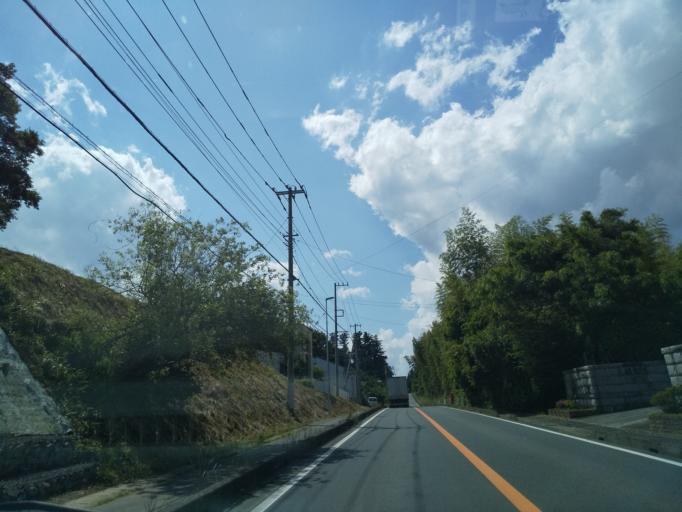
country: JP
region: Ibaraki
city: Ishioka
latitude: 36.1644
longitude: 140.3678
